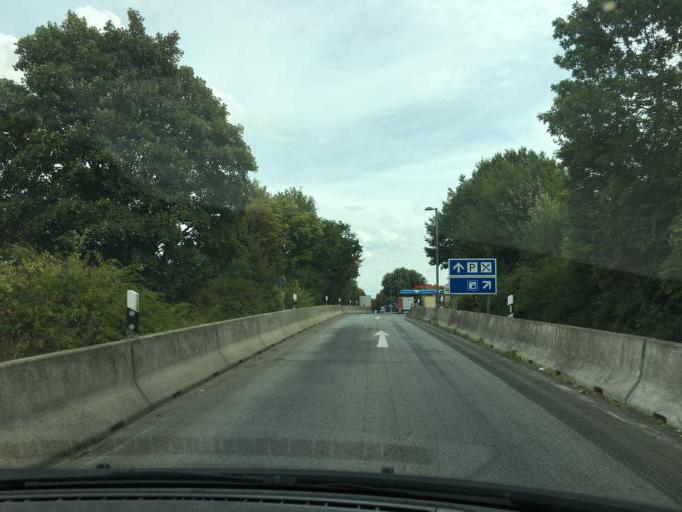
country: DE
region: North Rhine-Westphalia
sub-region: Regierungsbezirk Koln
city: Bedburg
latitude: 51.0056
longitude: 6.5179
